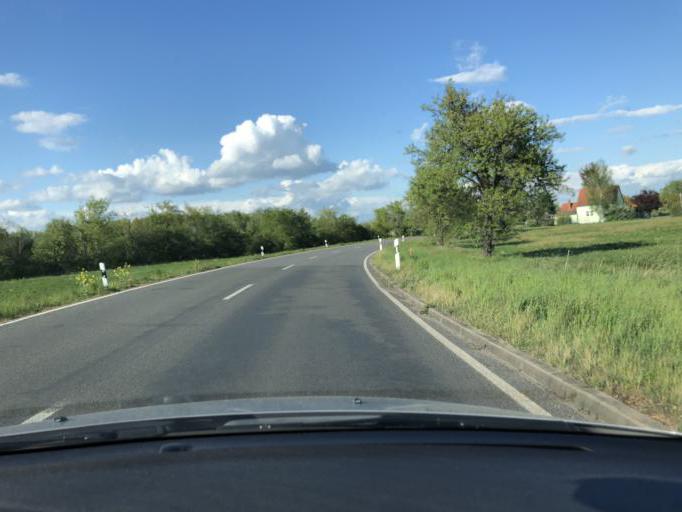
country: DE
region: Saxony
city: Deutzen
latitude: 51.1160
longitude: 12.4306
